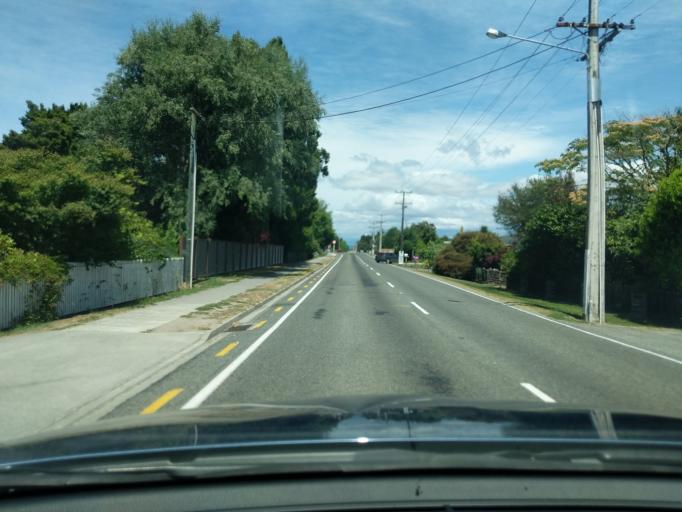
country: NZ
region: Tasman
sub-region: Tasman District
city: Motueka
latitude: -41.0786
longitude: 172.9974
